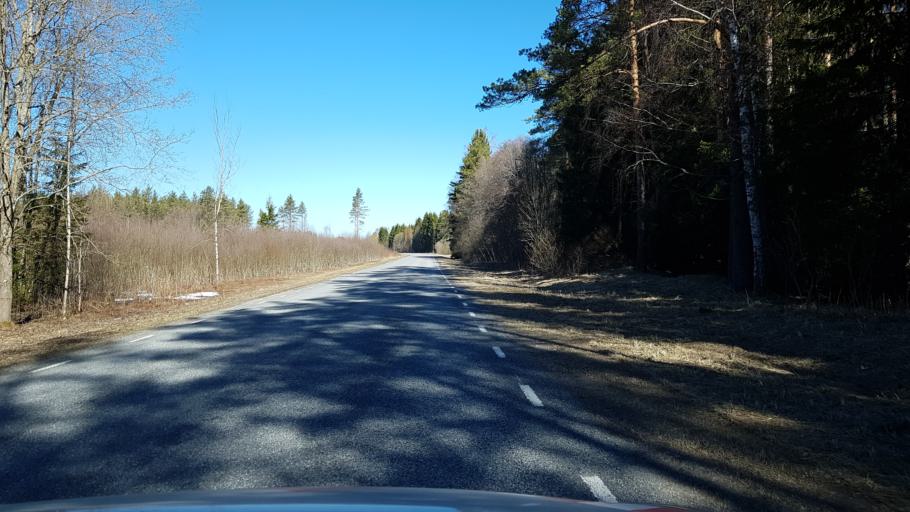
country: EE
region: Laeaene-Virumaa
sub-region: Haljala vald
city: Haljala
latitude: 59.5037
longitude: 26.2387
